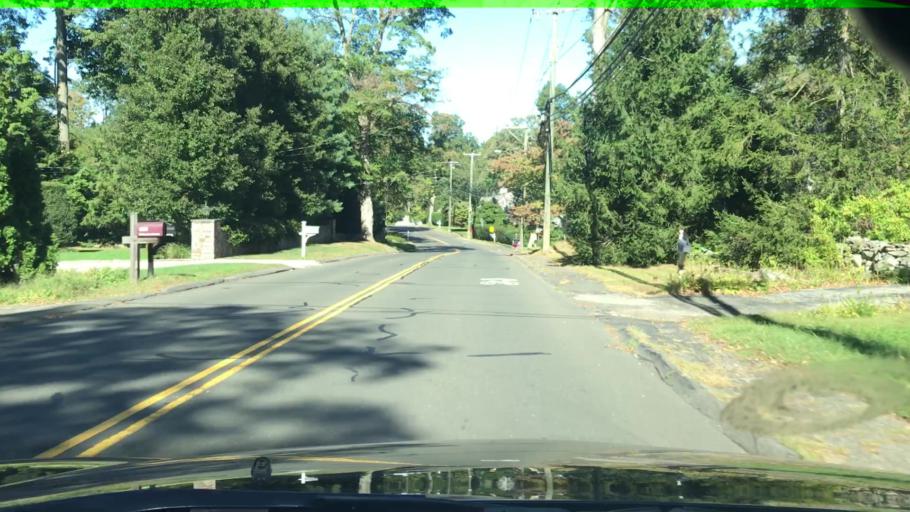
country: US
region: Connecticut
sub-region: Fairfield County
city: Darien
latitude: 41.0811
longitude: -73.4442
